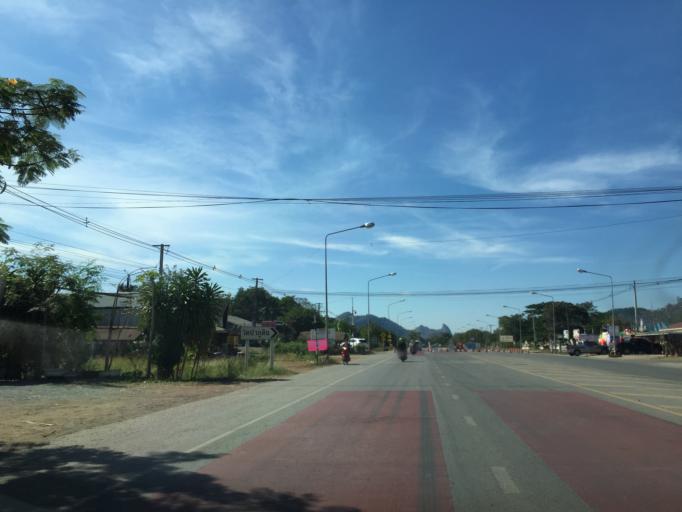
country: TH
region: Changwat Nong Bua Lamphu
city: Na Wang
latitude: 17.3253
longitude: 102.0677
